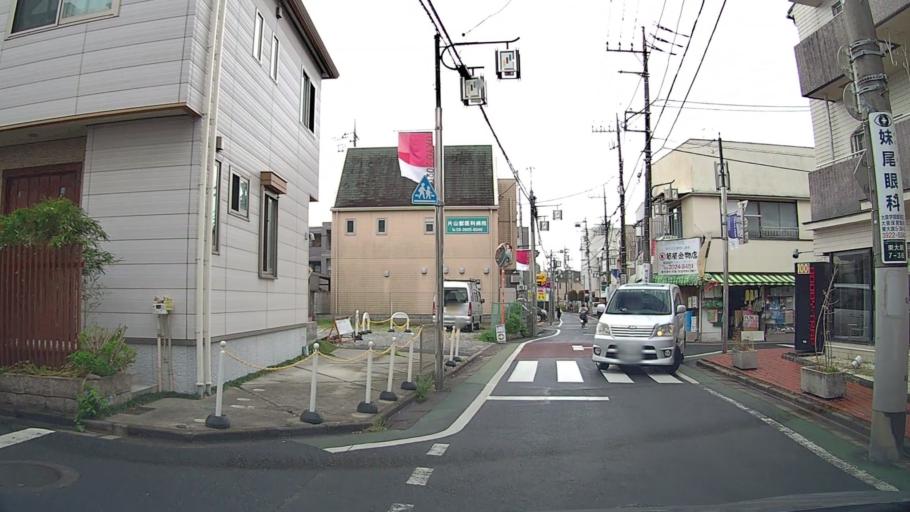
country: JP
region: Tokyo
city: Musashino
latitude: 35.7471
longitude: 139.5813
